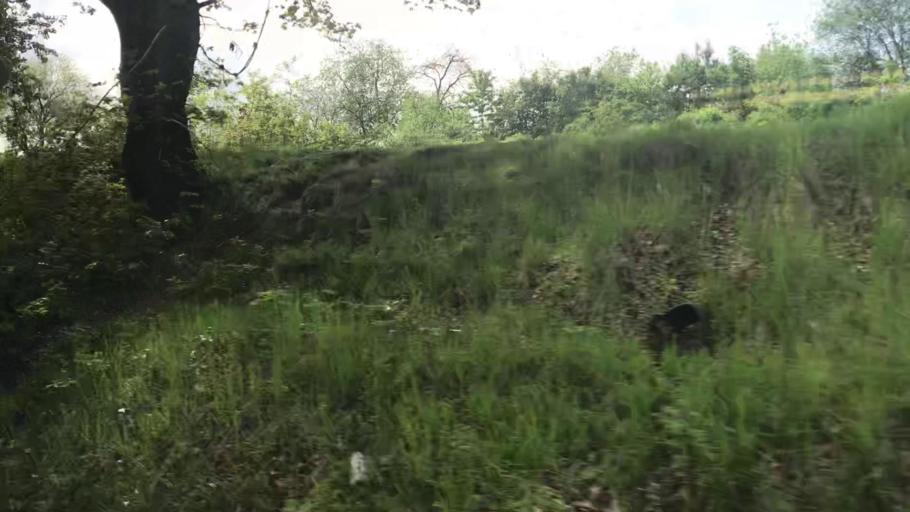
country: PL
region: Lower Silesian Voivodeship
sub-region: Powiat swidnicki
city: Swiebodzice
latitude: 50.8236
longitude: 16.3081
